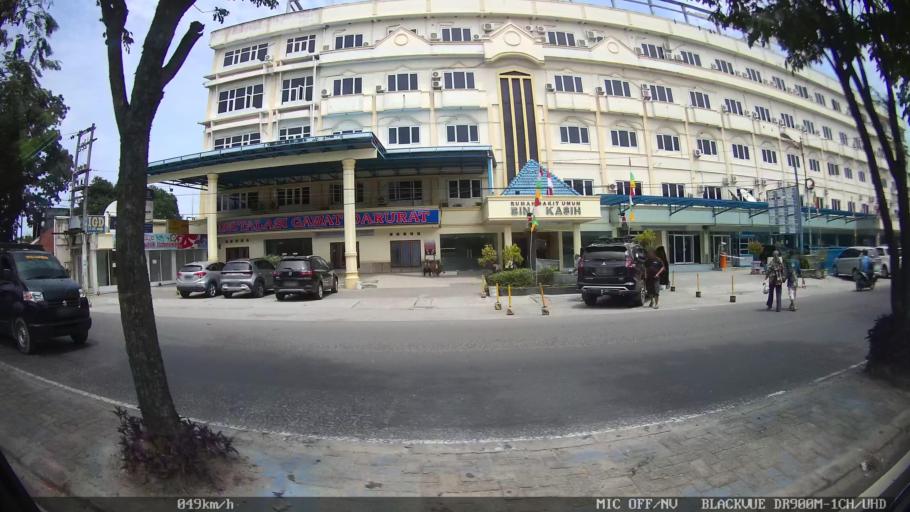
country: ID
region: North Sumatra
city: Sunggal
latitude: 3.5792
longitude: 98.6138
